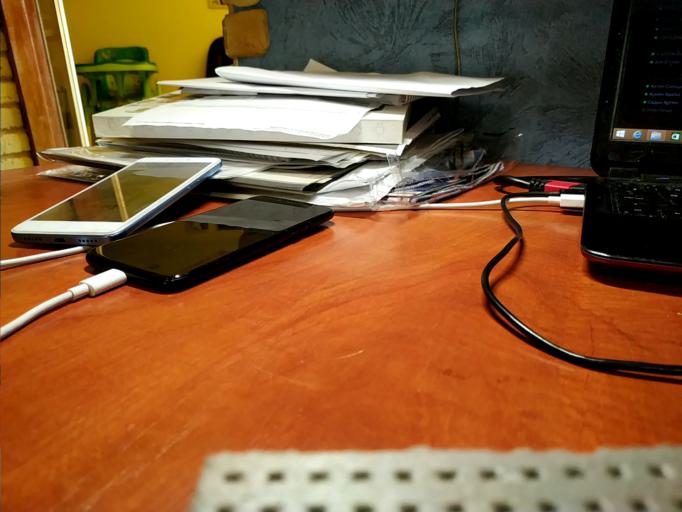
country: RU
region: Tverskaya
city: Spirovo
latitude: 57.4251
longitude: 35.0796
